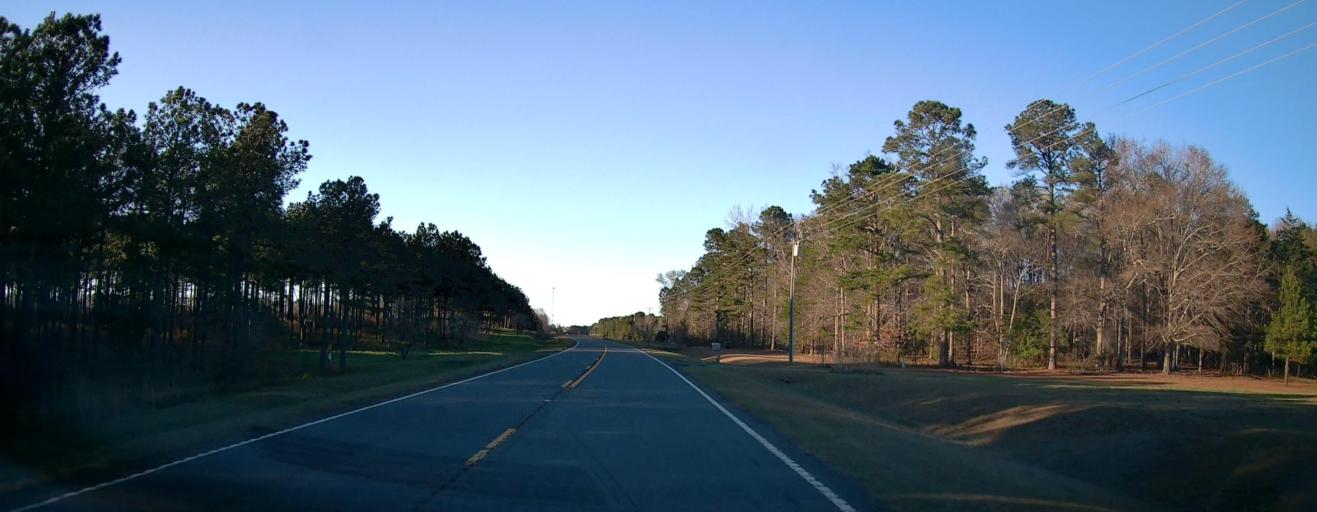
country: US
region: Georgia
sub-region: Talbot County
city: Talbotton
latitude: 32.6382
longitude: -84.5373
